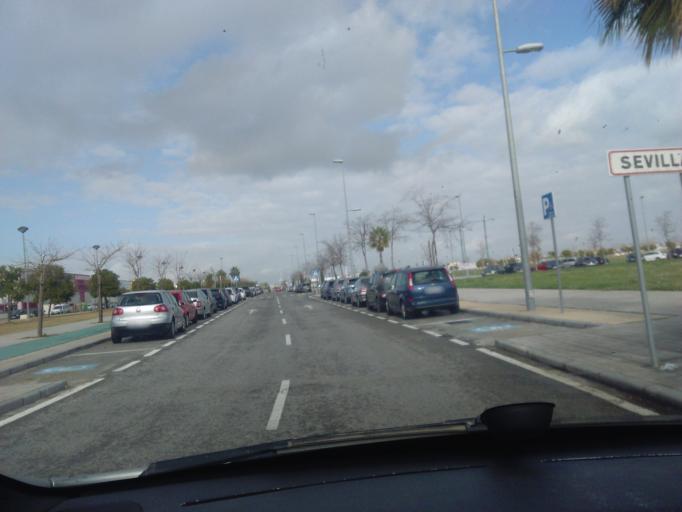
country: ES
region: Andalusia
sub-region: Provincia de Sevilla
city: Sevilla
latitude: 37.3755
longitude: -5.9144
